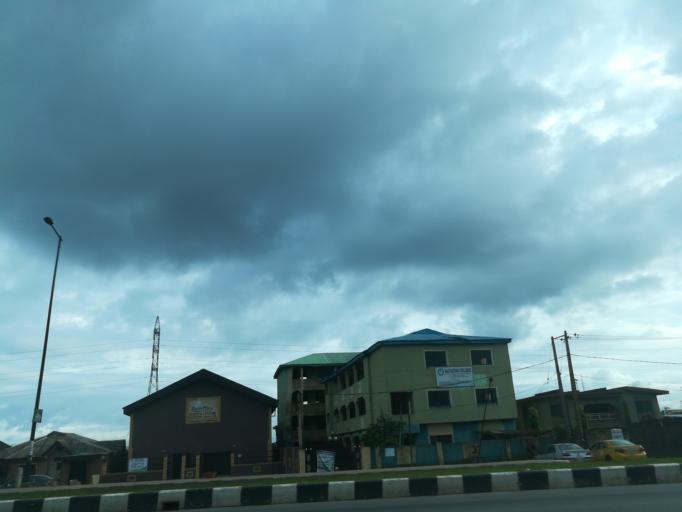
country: NG
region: Lagos
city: Ebute Ikorodu
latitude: 6.6094
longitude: 3.4333
